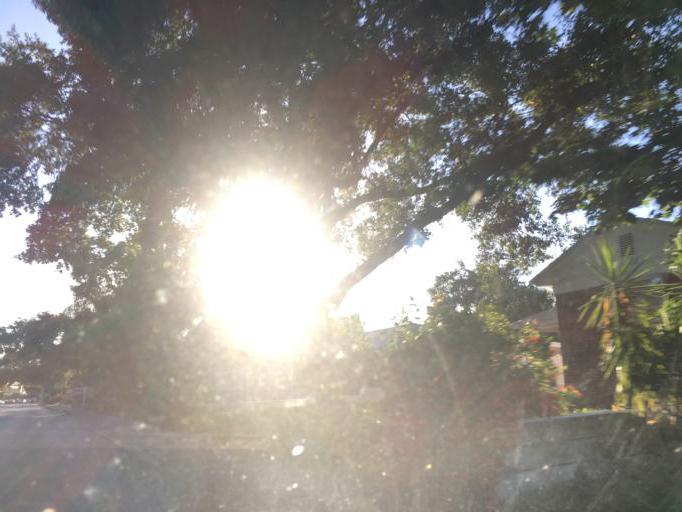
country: US
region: Florida
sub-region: Pinellas County
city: Saint Petersburg
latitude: 27.7921
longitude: -82.6358
